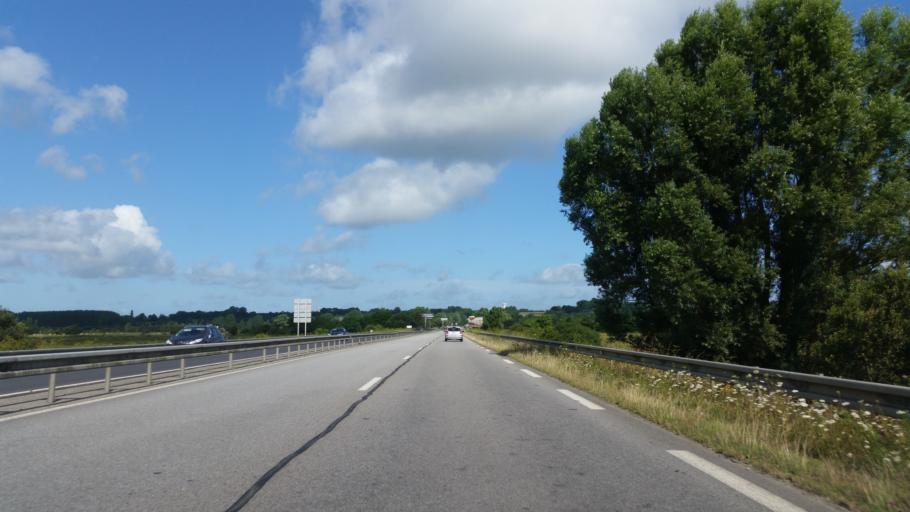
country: FR
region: Lower Normandy
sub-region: Departement de la Manche
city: Carentan
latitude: 49.3245
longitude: -1.2486
